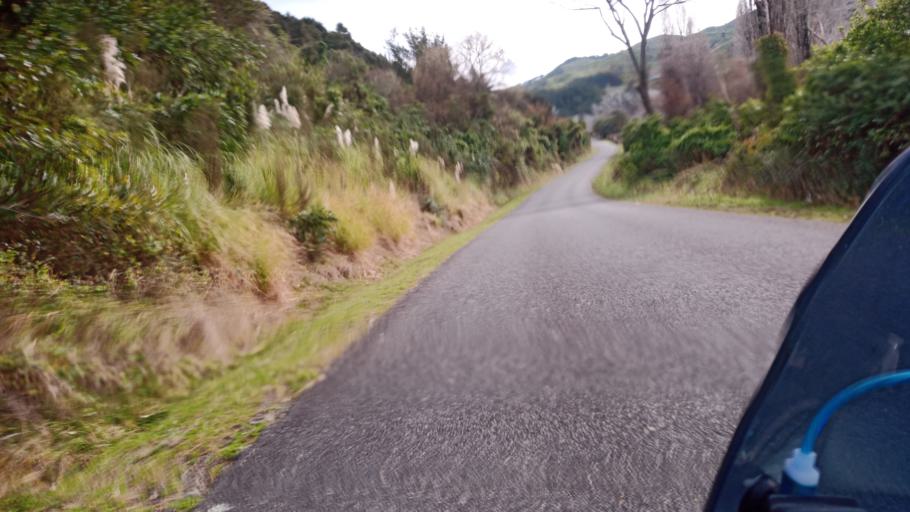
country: NZ
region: Hawke's Bay
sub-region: Wairoa District
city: Wairoa
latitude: -38.8289
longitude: 177.5163
